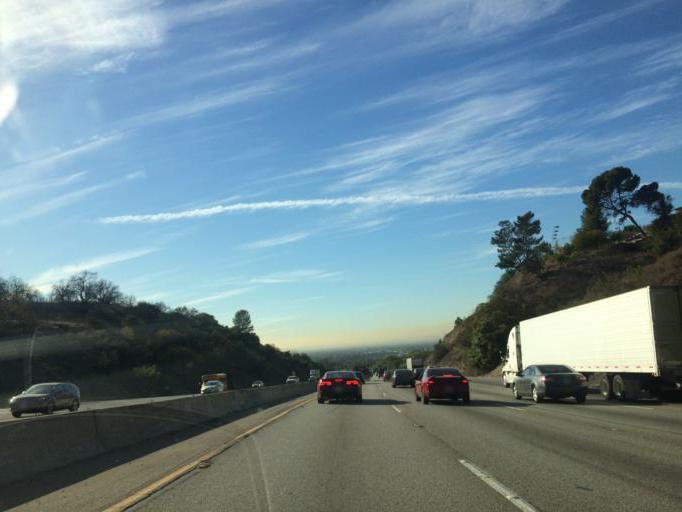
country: US
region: California
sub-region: Los Angeles County
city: Charter Oak
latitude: 34.0683
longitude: -117.8469
